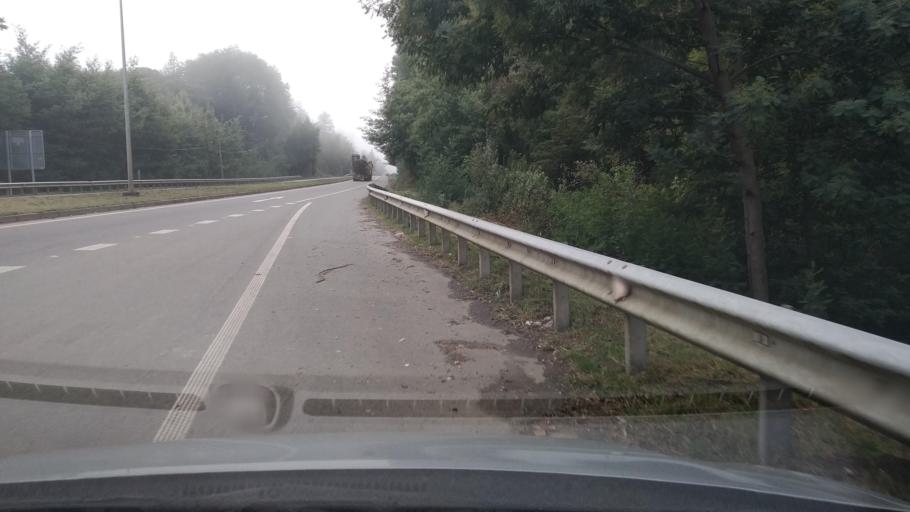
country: CL
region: Los Lagos
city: Las Animas
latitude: -39.7603
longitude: -73.2283
